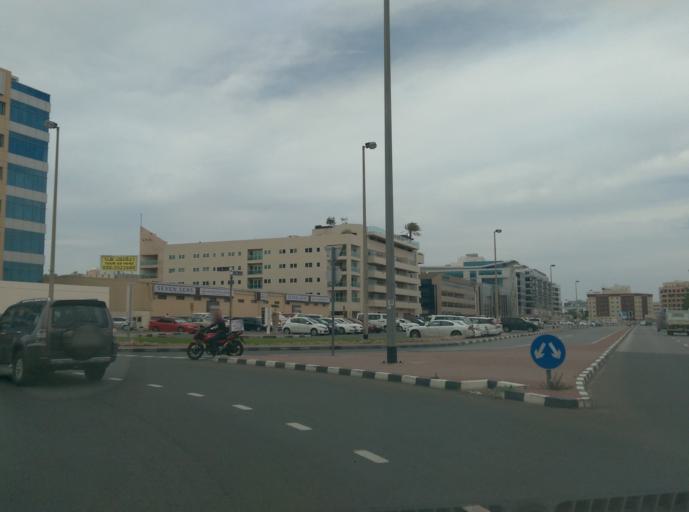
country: AE
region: Ash Shariqah
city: Sharjah
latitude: 25.2410
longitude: 55.3101
